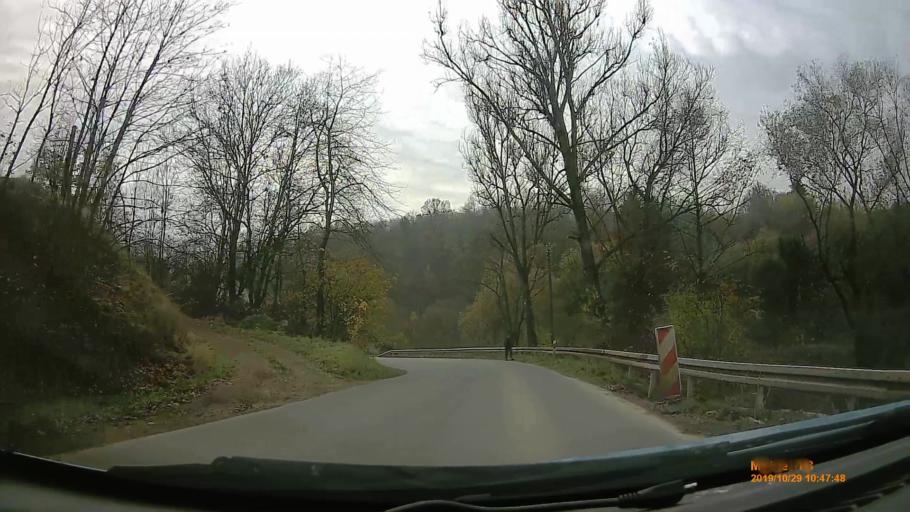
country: PL
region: Lower Silesian Voivodeship
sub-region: Powiat klodzki
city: Radkow
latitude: 50.5530
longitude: 16.4356
